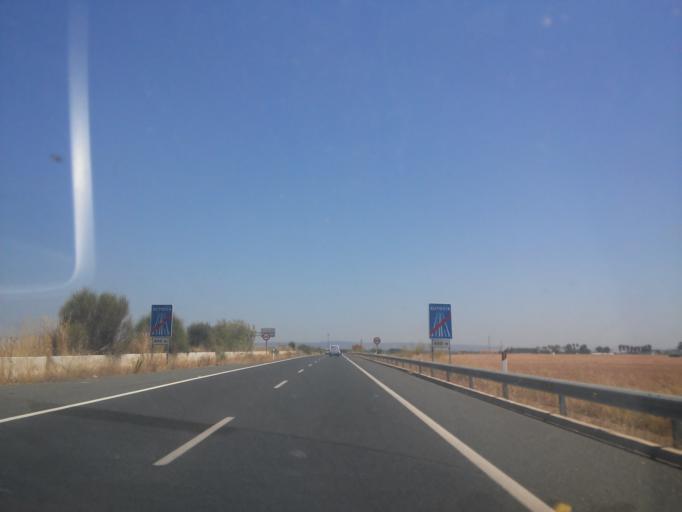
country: ES
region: Andalusia
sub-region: Provincia de Sevilla
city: La Rinconada
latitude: 37.4604
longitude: -5.9690
